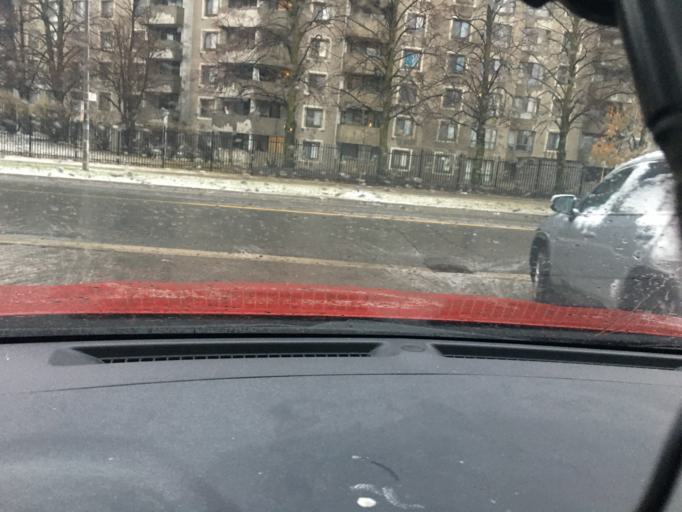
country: CA
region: Ontario
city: Scarborough
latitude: 43.8081
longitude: -79.2705
